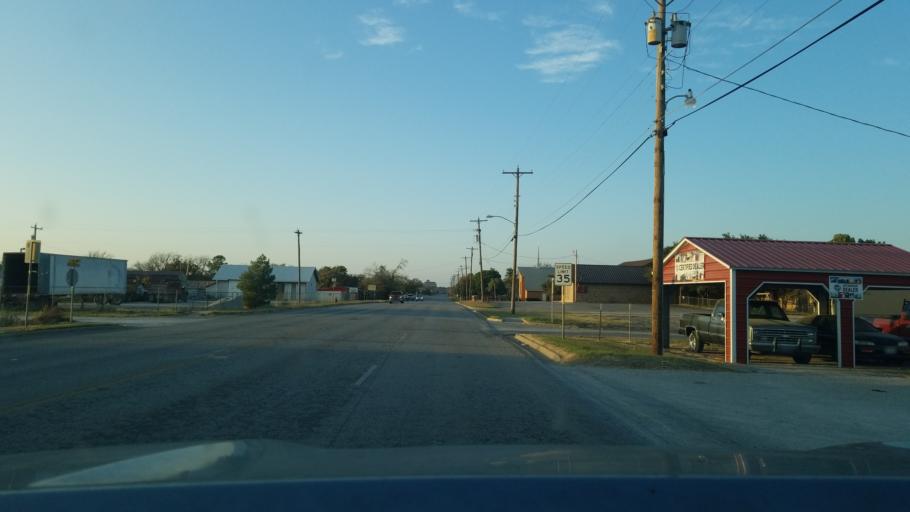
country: US
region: Texas
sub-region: Eastland County
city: Cisco
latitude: 32.3783
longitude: -98.9729
